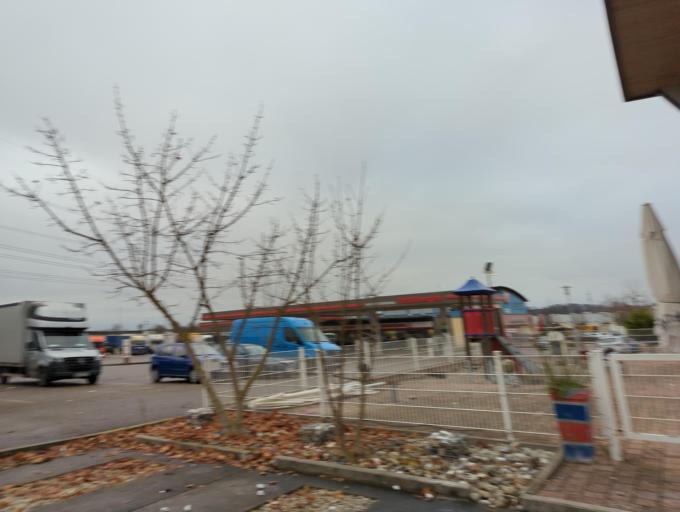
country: DE
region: Bavaria
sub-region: Swabia
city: Wasserburg
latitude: 48.4279
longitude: 10.2885
